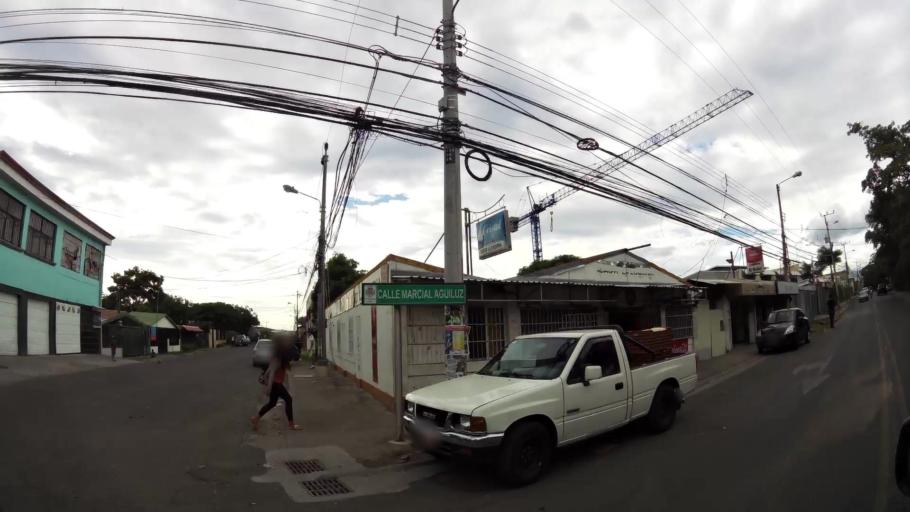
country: CR
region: San Jose
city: Santa Ana
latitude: 9.9508
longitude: -84.1895
